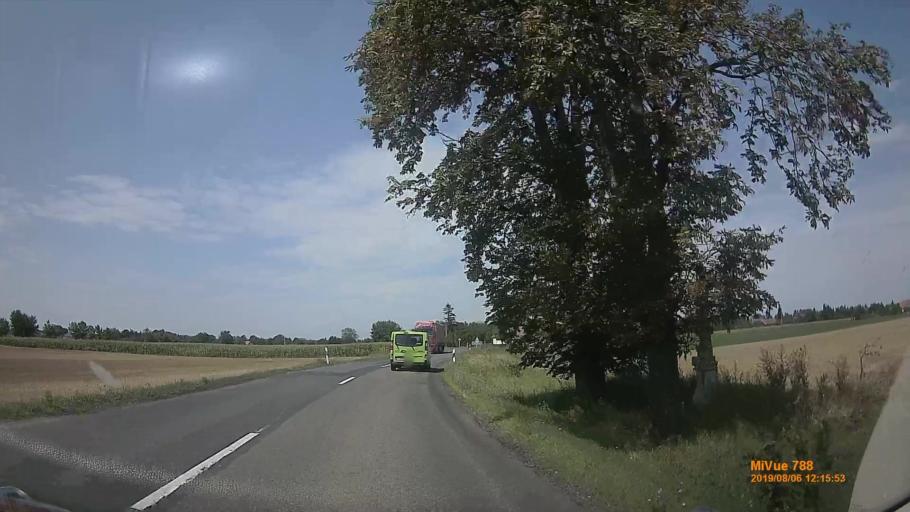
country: HU
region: Vas
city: Vasvar
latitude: 47.1516
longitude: 16.8114
